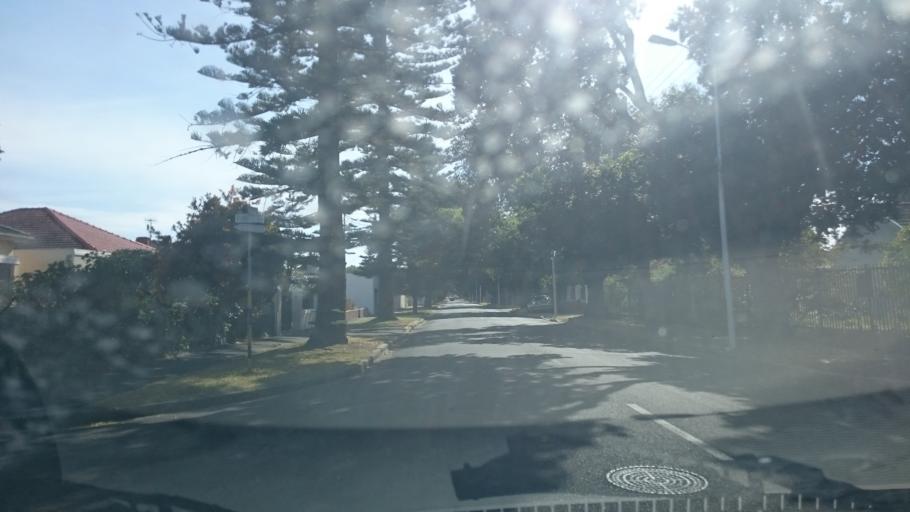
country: ZA
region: Western Cape
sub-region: City of Cape Town
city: Lansdowne
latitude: -34.0185
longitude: 18.4791
